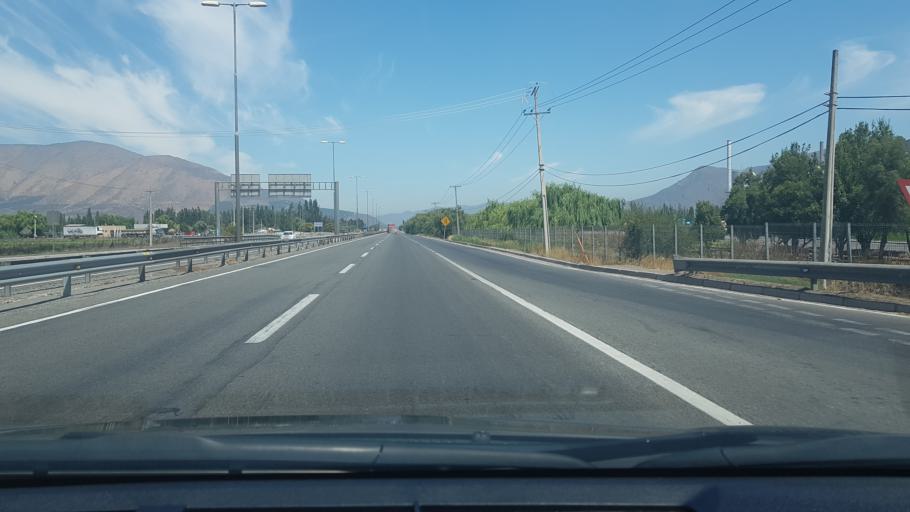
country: CL
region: Valparaiso
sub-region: Provincia de San Felipe
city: Llaillay
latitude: -32.8508
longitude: -70.9438
